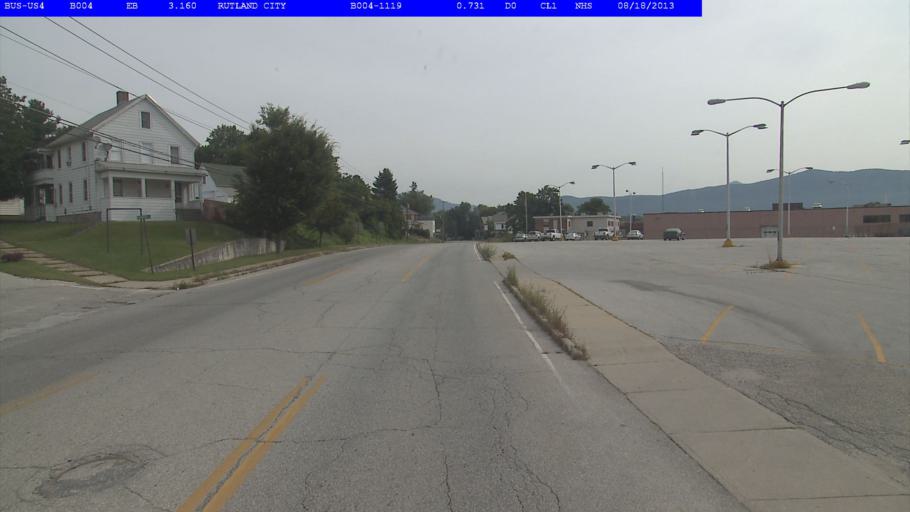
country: US
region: Vermont
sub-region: Rutland County
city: Rutland
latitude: 43.6064
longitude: -72.9934
